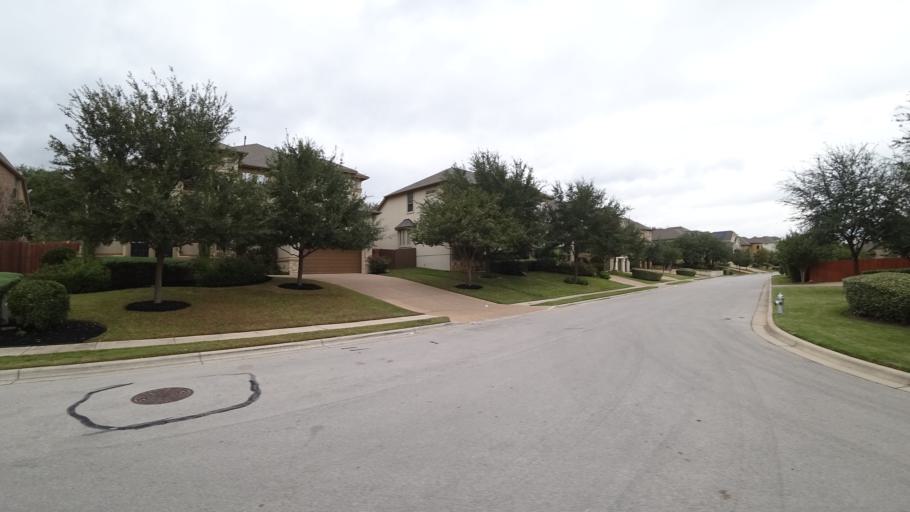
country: US
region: Texas
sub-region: Travis County
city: Bee Cave
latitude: 30.3404
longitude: -97.9087
